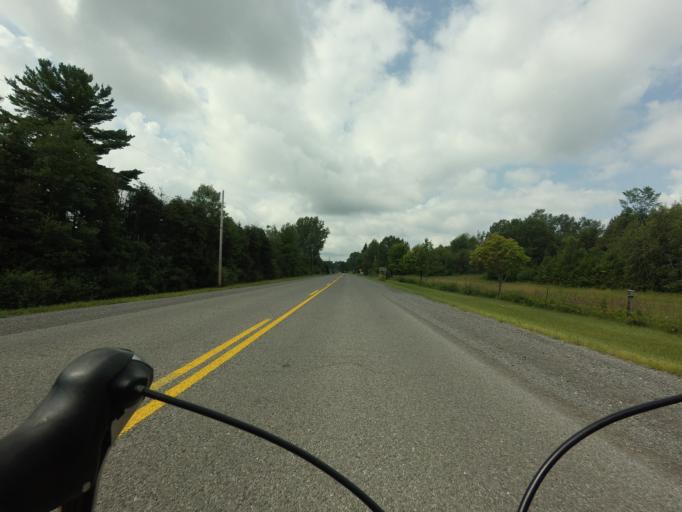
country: CA
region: Ontario
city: Brockville
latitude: 44.7550
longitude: -75.7300
